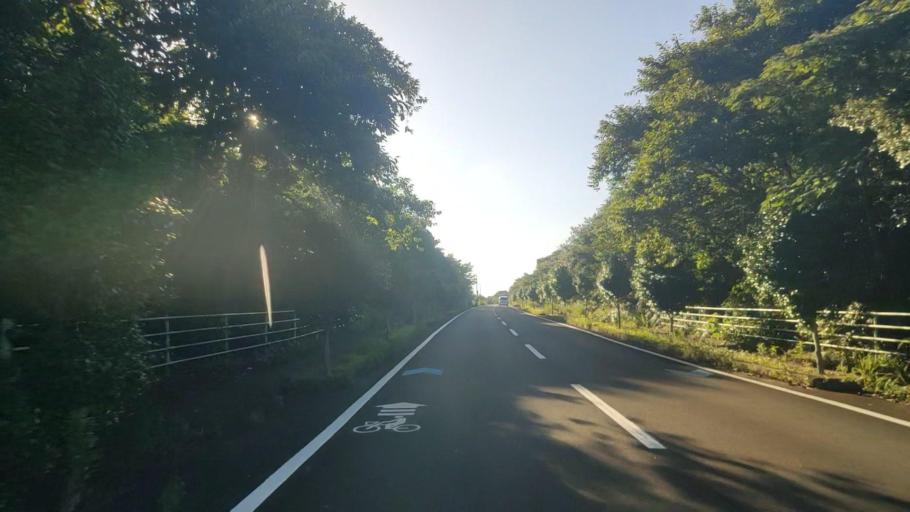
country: JP
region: Mie
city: Toba
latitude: 34.2721
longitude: 136.7812
